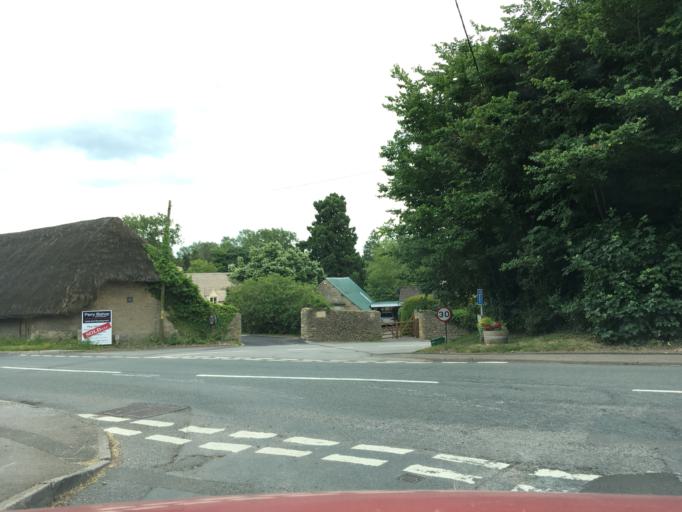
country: GB
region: England
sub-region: Gloucestershire
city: Cirencester
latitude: 51.7335
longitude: -1.9837
